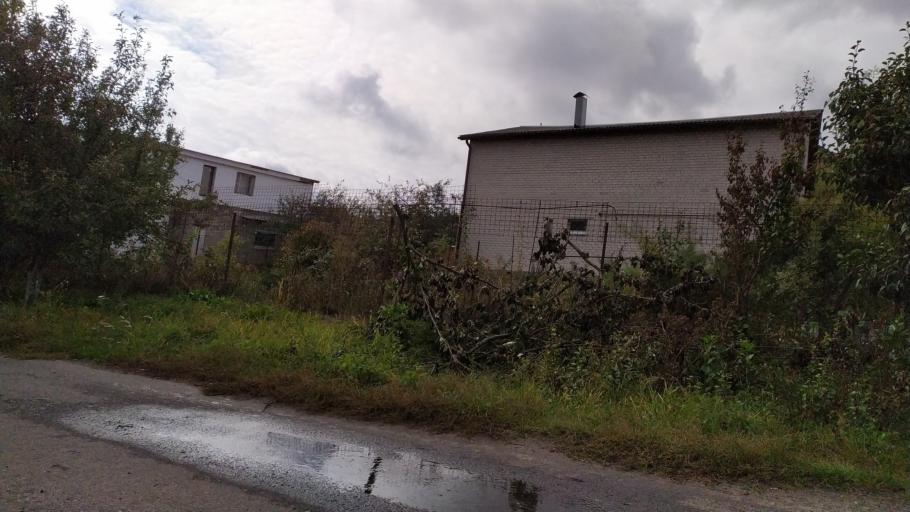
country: RU
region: Kursk
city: Kursk
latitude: 51.6431
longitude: 36.1551
